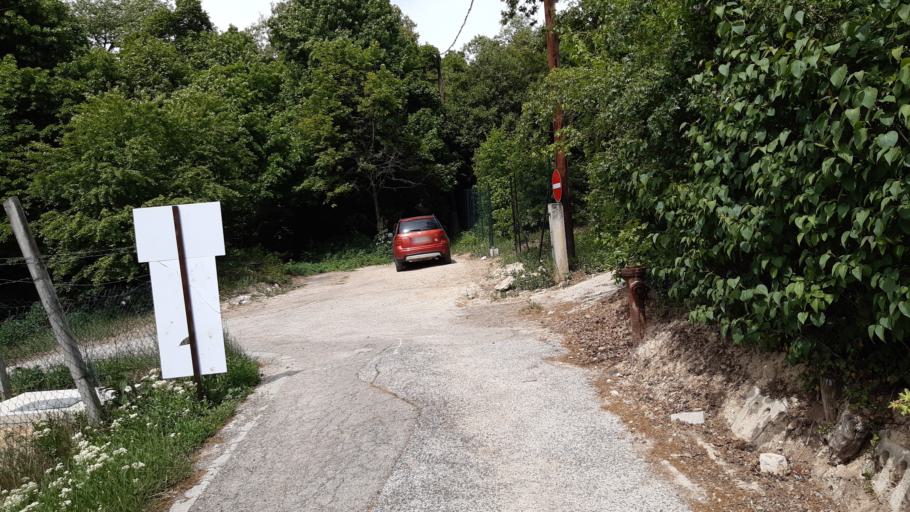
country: HU
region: Pest
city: Budaors
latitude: 47.4849
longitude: 18.9675
